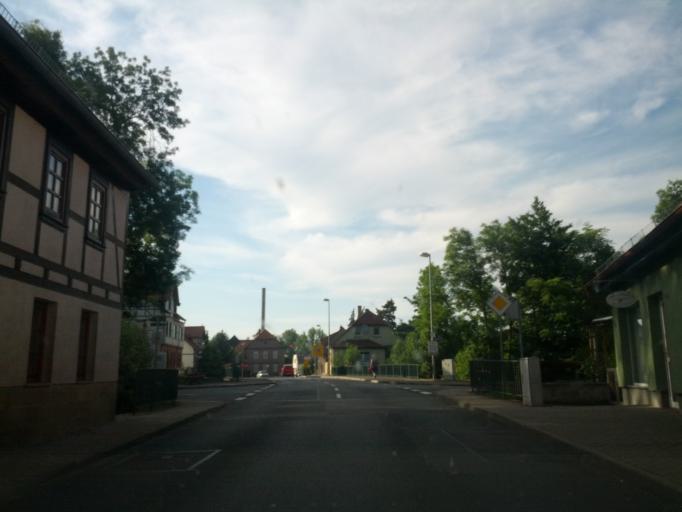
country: DE
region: Thuringia
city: Seebergen
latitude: 50.8931
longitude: 10.7761
